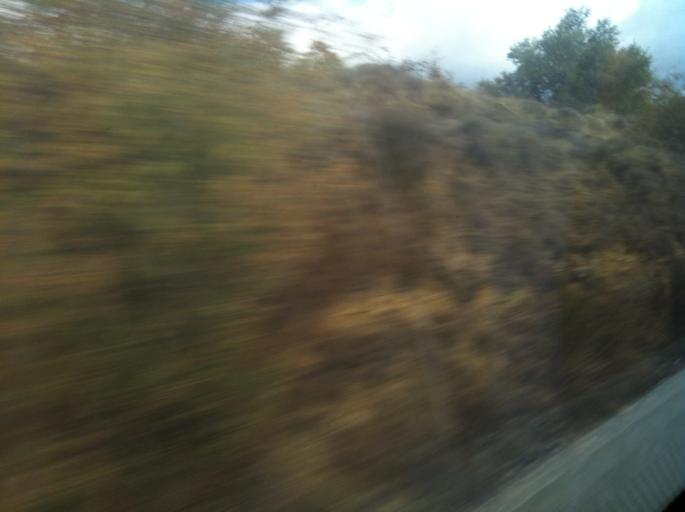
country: ES
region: Basque Country
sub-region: Provincia de Alava
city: Arminon
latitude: 42.7014
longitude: -2.8977
